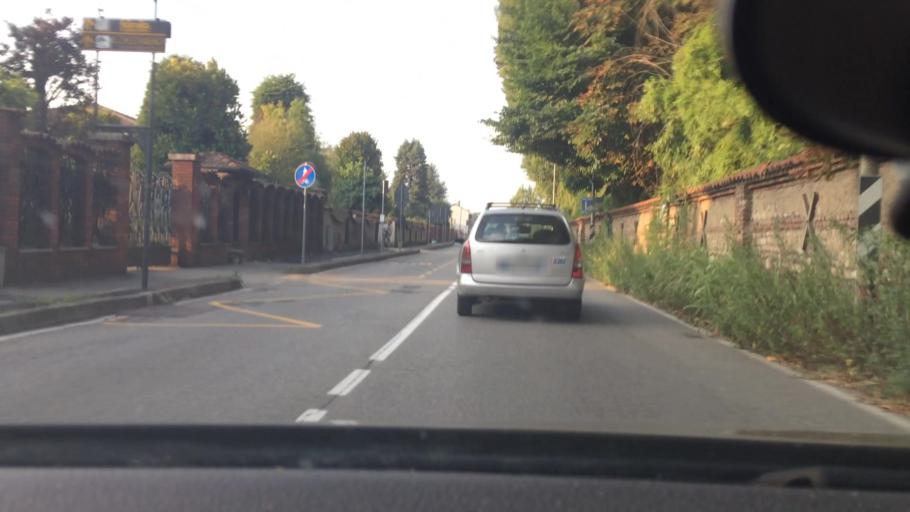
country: IT
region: Lombardy
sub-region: Citta metropolitana di Milano
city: Casorezzo
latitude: 45.5232
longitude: 8.9058
